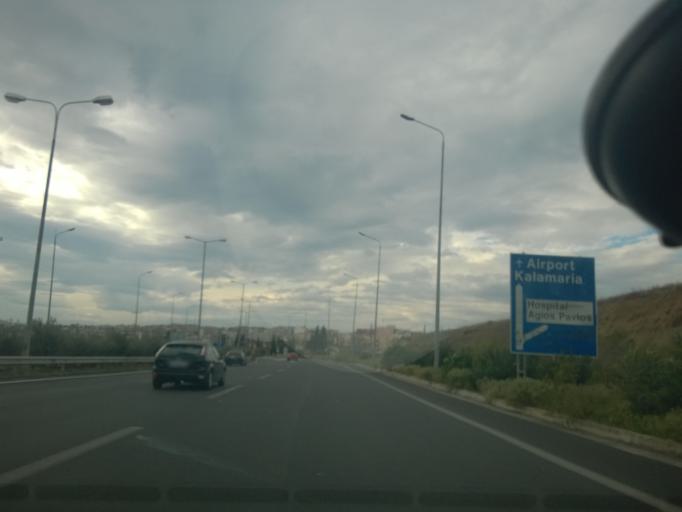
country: GR
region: Central Macedonia
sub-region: Nomos Thessalonikis
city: Kalamaria
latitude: 40.5792
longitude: 22.9735
